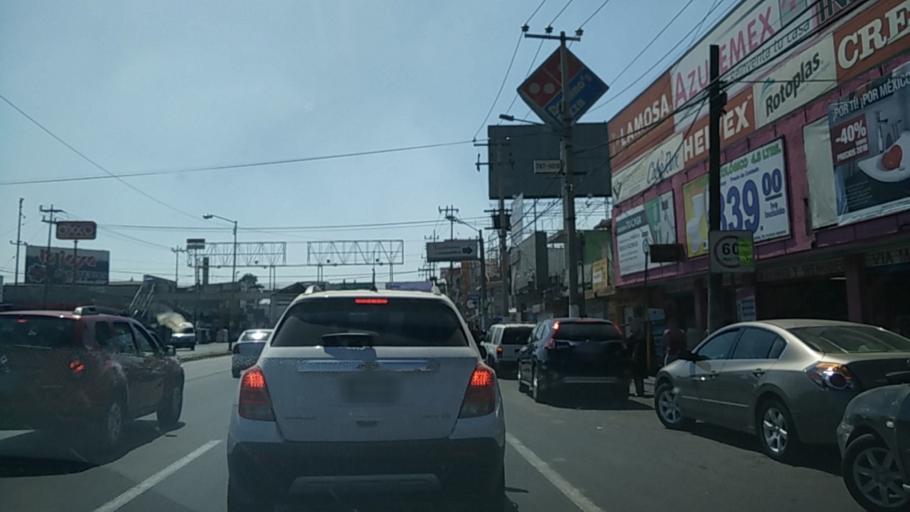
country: MX
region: Mexico
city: Ecatepec
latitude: 19.5935
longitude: -99.0386
